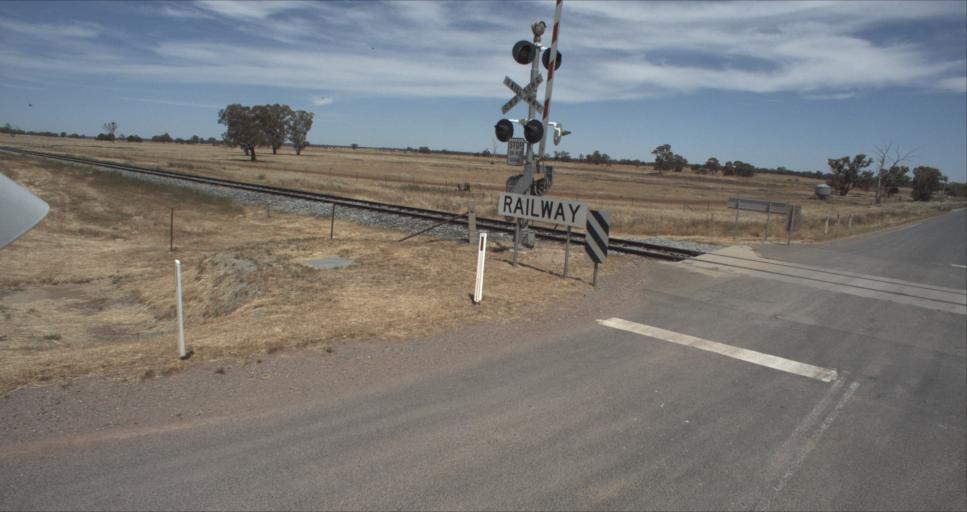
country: AU
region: New South Wales
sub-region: Leeton
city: Leeton
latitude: -34.6471
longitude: 146.4723
